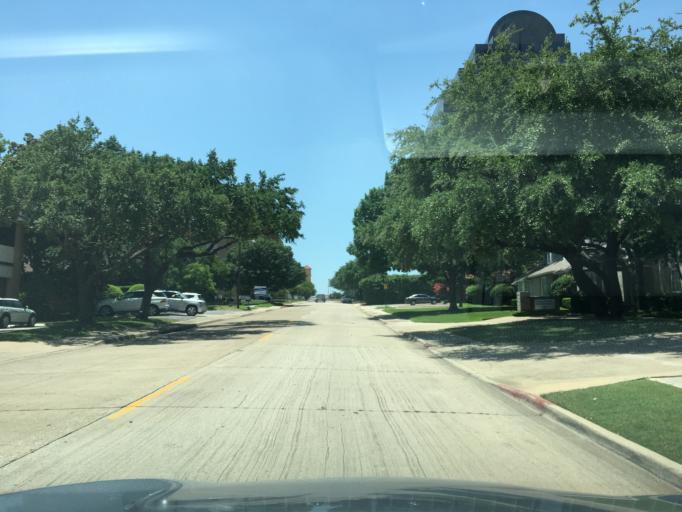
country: US
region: Texas
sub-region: Dallas County
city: University Park
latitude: 32.8833
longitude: -96.7669
